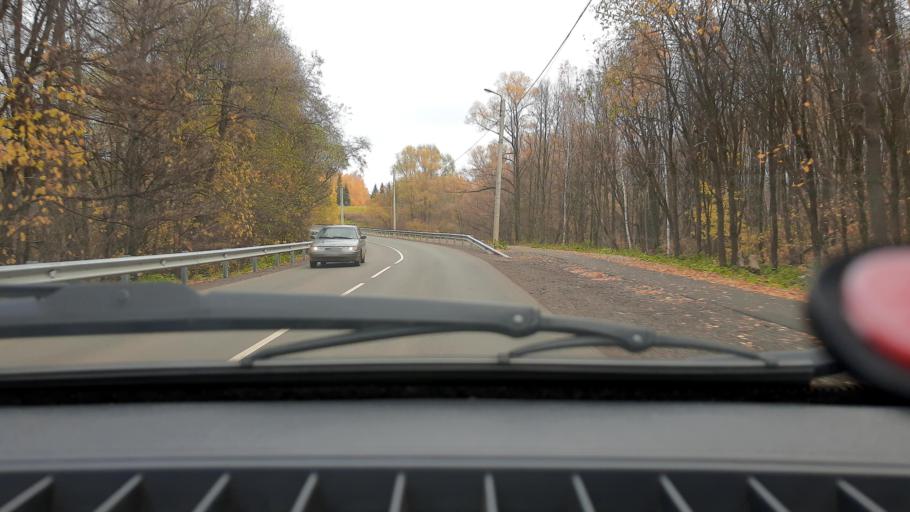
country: RU
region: Bashkortostan
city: Avdon
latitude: 54.6641
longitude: 55.7089
